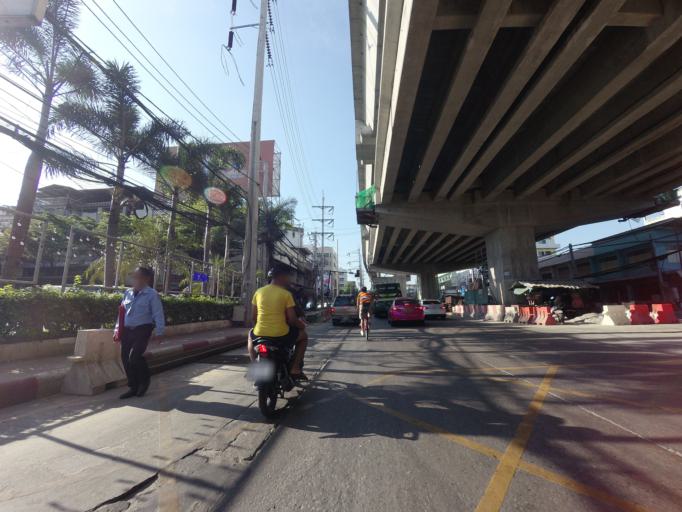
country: TH
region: Samut Prakan
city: Samut Prakan
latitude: 13.6459
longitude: 100.5956
